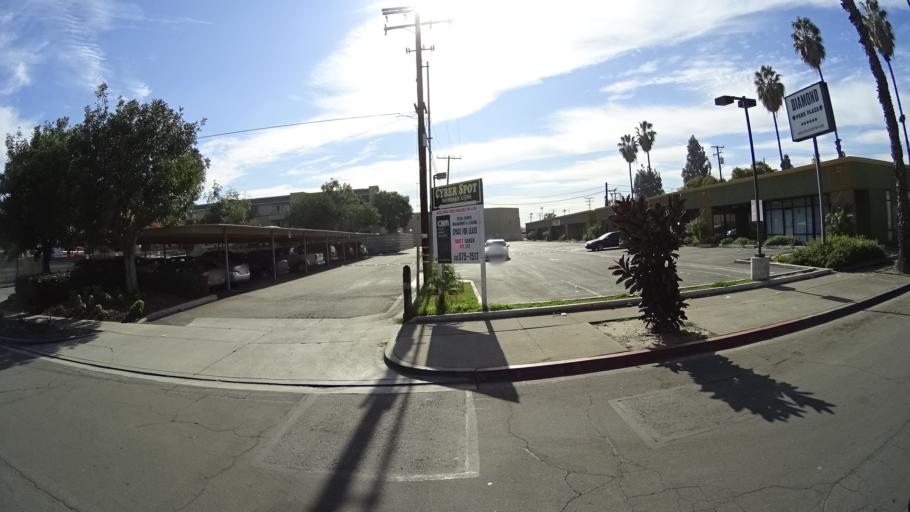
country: US
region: California
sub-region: Orange County
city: Stanton
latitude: 33.8209
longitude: -117.9603
